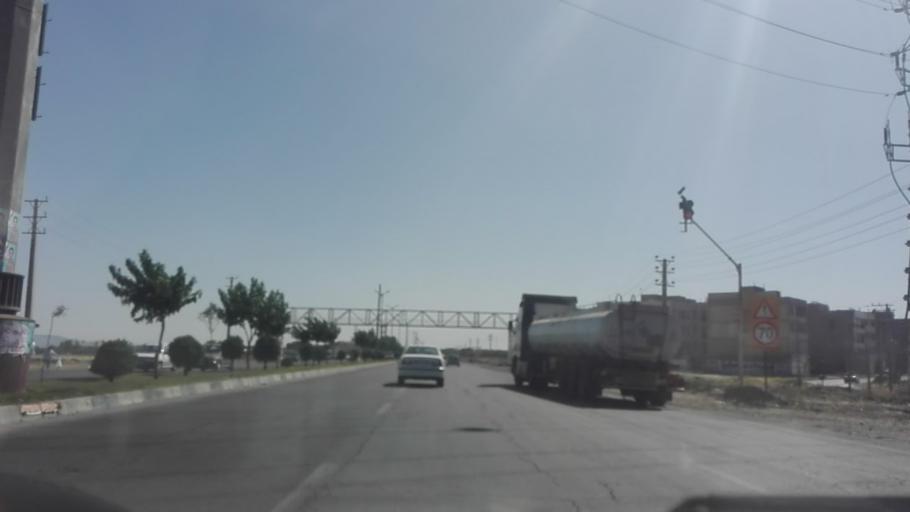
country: IR
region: Tehran
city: Shahre Jadide Andisheh
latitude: 35.6606
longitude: 51.0127
